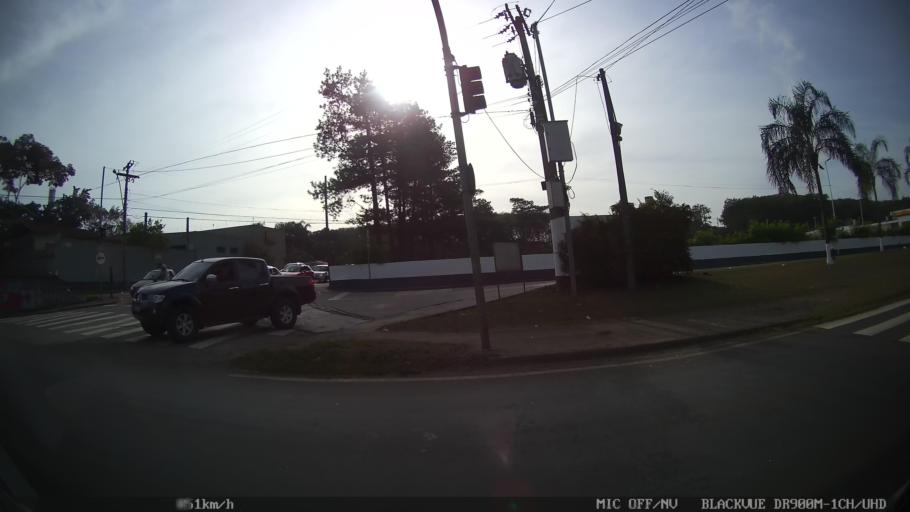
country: BR
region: Sao Paulo
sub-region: Piracicaba
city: Piracicaba
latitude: -22.6968
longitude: -47.6609
